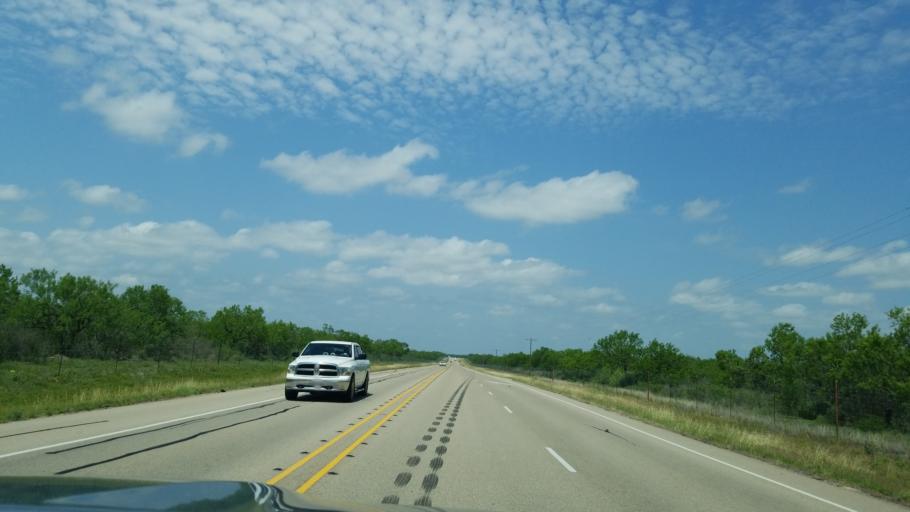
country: US
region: Texas
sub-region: Frio County
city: Pearsall
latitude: 29.0076
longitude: -99.1844
